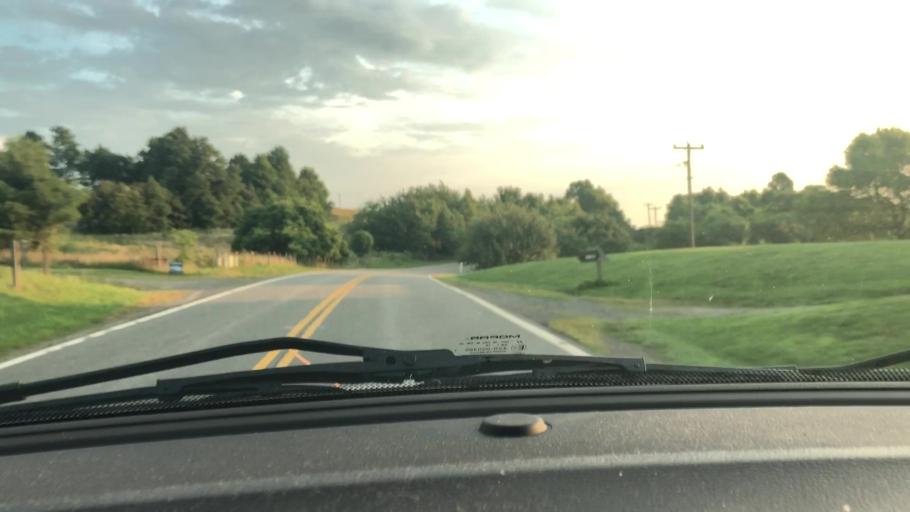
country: US
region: Virginia
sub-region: Patrick County
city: Stuart
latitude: 36.7156
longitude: -80.3344
